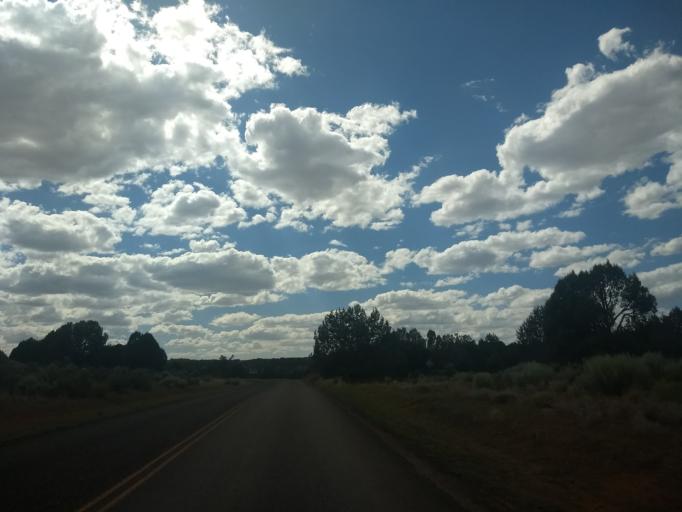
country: US
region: Utah
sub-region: Kane County
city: Kanab
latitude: 37.1452
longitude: -112.5622
